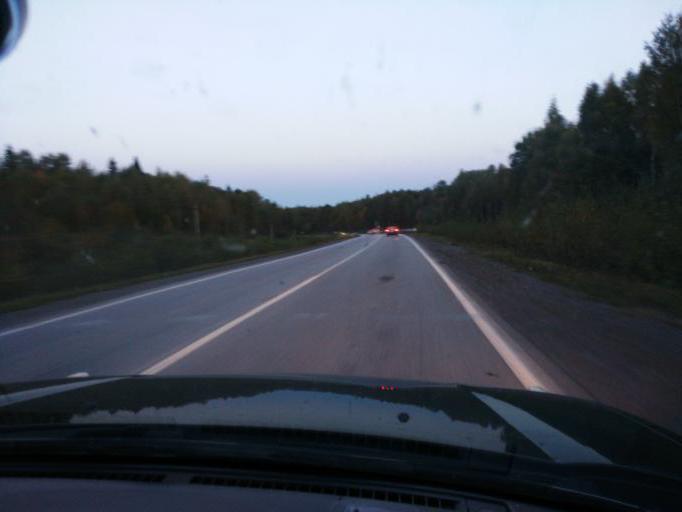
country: RU
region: Perm
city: Verkhnechusovskiye Gorodki
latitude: 58.2459
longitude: 57.0256
